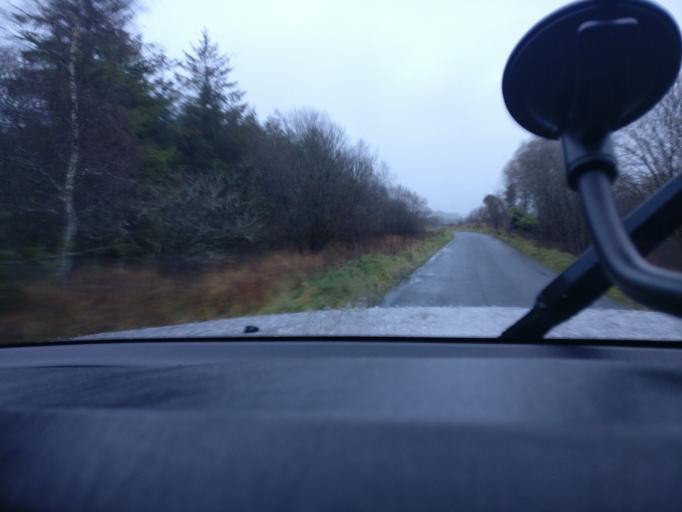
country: IE
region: Connaught
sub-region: County Galway
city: Loughrea
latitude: 53.2329
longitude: -8.5264
